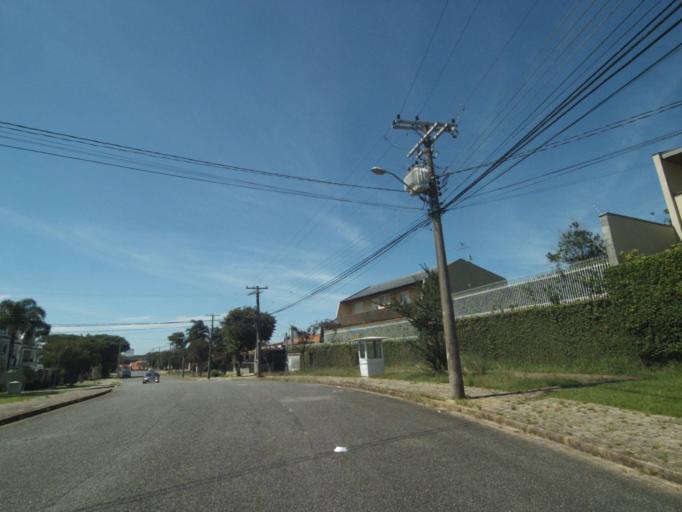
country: BR
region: Parana
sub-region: Curitiba
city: Curitiba
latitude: -25.4579
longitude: -49.2446
